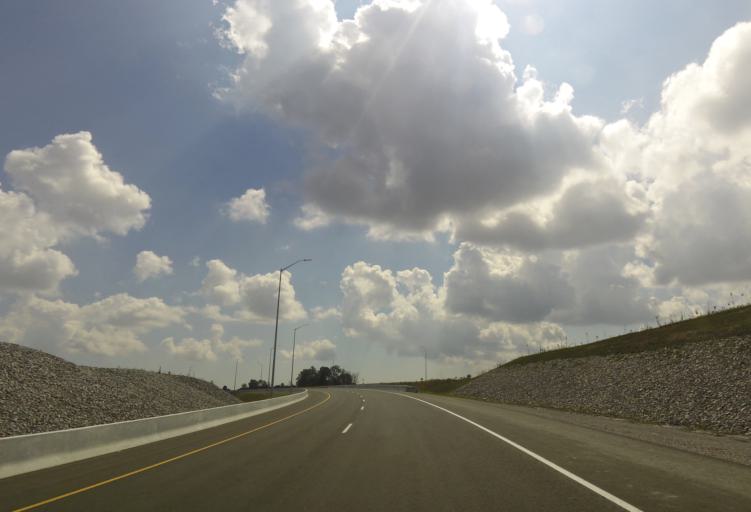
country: CA
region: Ontario
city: Ajax
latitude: 43.9501
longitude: -79.0099
